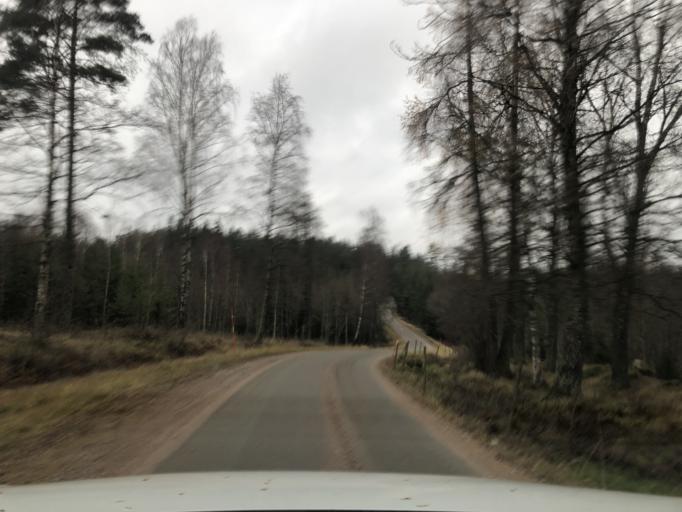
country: SE
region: Vaestra Goetaland
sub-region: Ulricehamns Kommun
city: Ulricehamn
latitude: 57.8532
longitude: 13.6323
